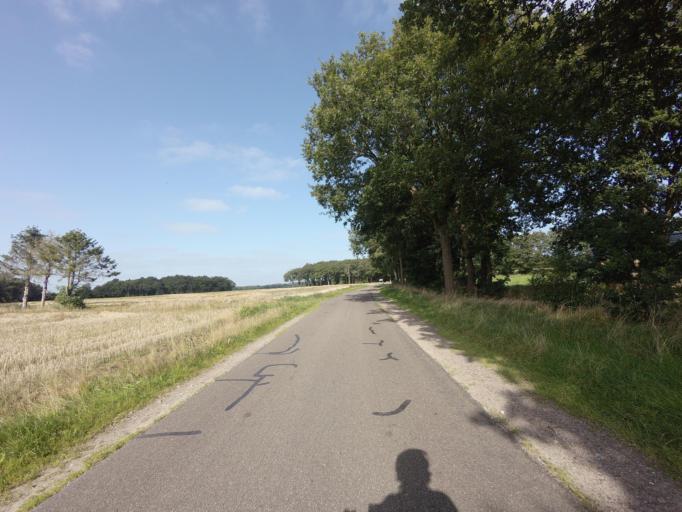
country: NL
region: Drenthe
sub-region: Gemeente Assen
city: Assen
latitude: 53.0495
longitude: 6.4686
